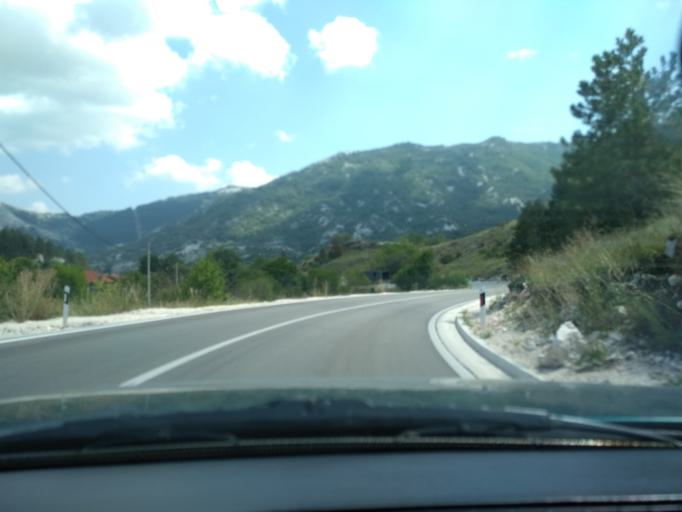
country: ME
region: Kotor
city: Kotor
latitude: 42.4276
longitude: 18.8183
